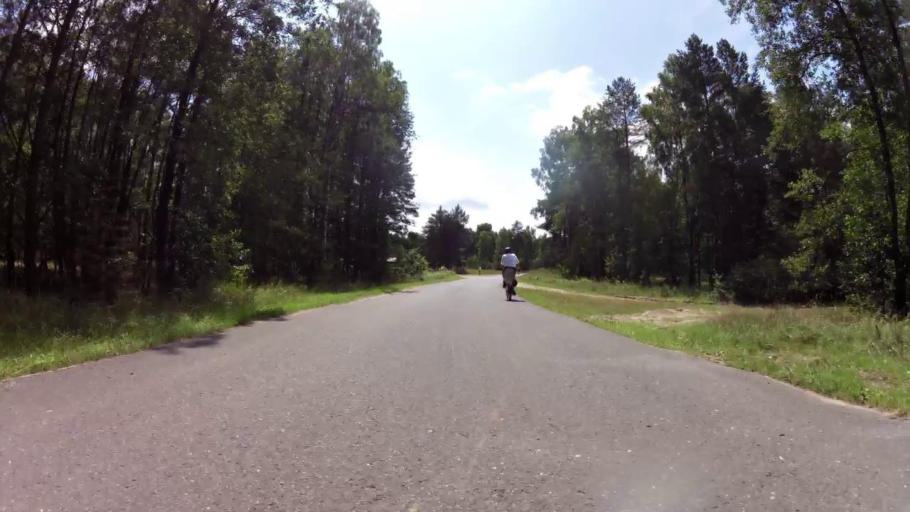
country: PL
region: West Pomeranian Voivodeship
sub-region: Powiat choszczenski
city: Drawno
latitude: 53.3785
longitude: 15.7290
